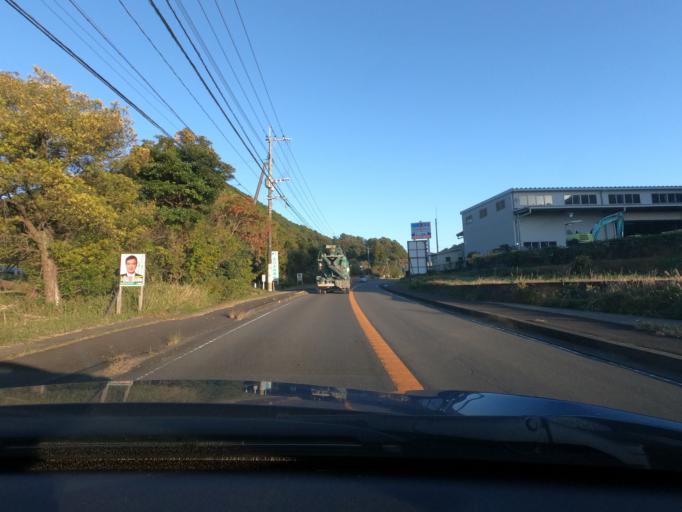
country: JP
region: Kagoshima
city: Satsumasendai
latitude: 31.8054
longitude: 130.3530
